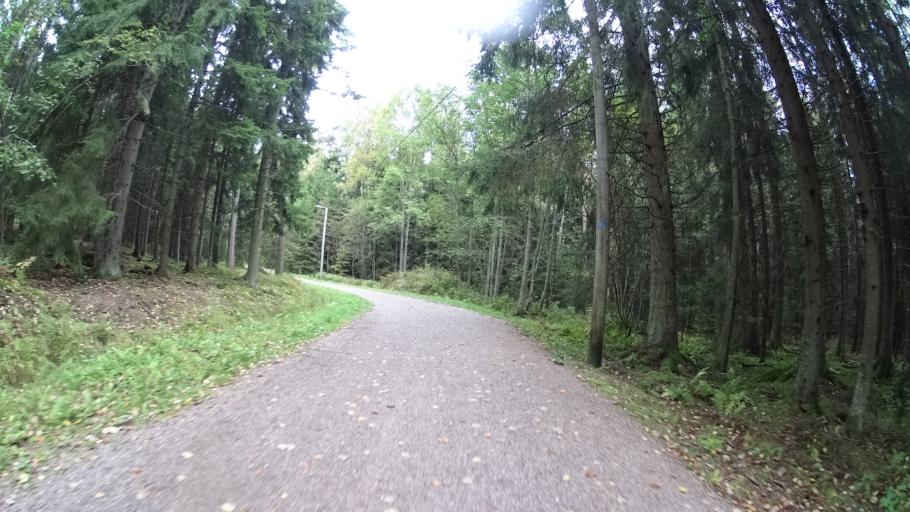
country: FI
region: Uusimaa
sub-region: Helsinki
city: Kauniainen
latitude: 60.1903
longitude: 24.7071
